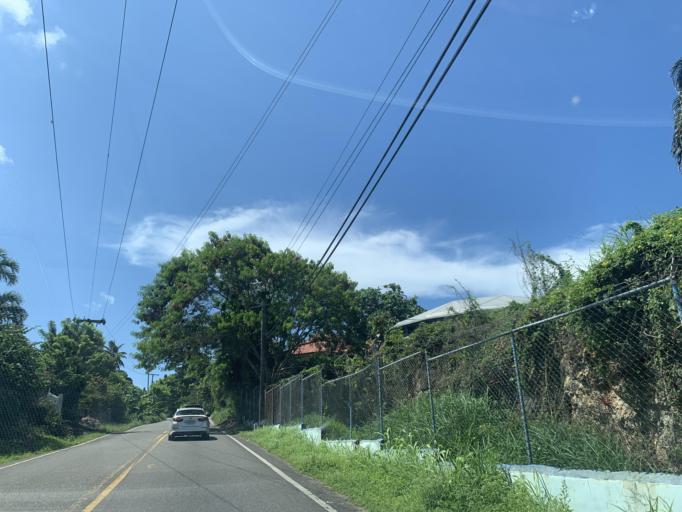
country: DO
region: Maria Trinidad Sanchez
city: Cabrera
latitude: 19.6499
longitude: -69.9297
